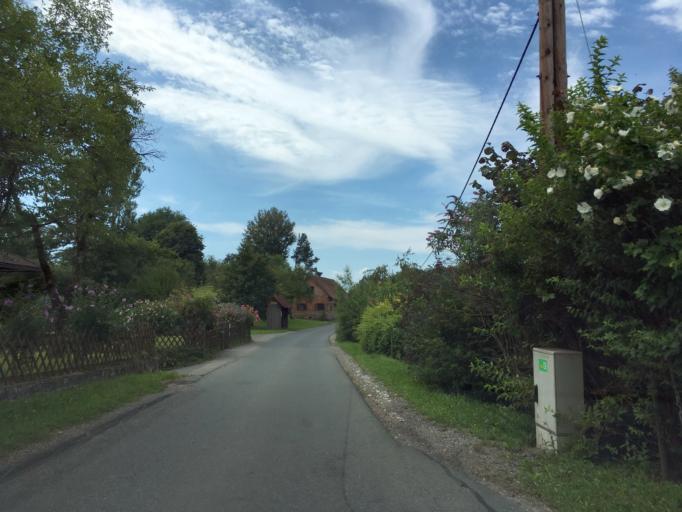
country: AT
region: Styria
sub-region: Politischer Bezirk Leibnitz
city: Pistorf
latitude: 46.7776
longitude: 15.3977
